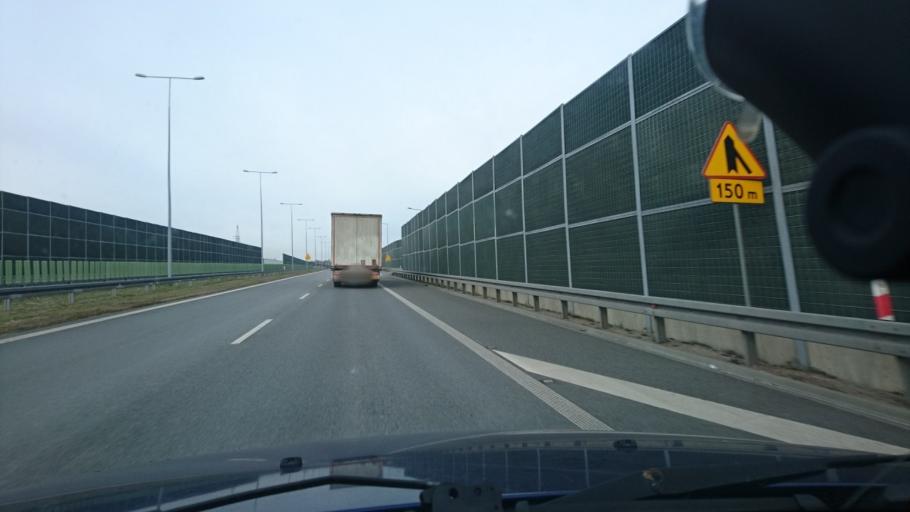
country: PL
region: Silesian Voivodeship
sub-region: Powiat bielski
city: Wilkowice
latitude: 49.7614
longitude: 19.0845
